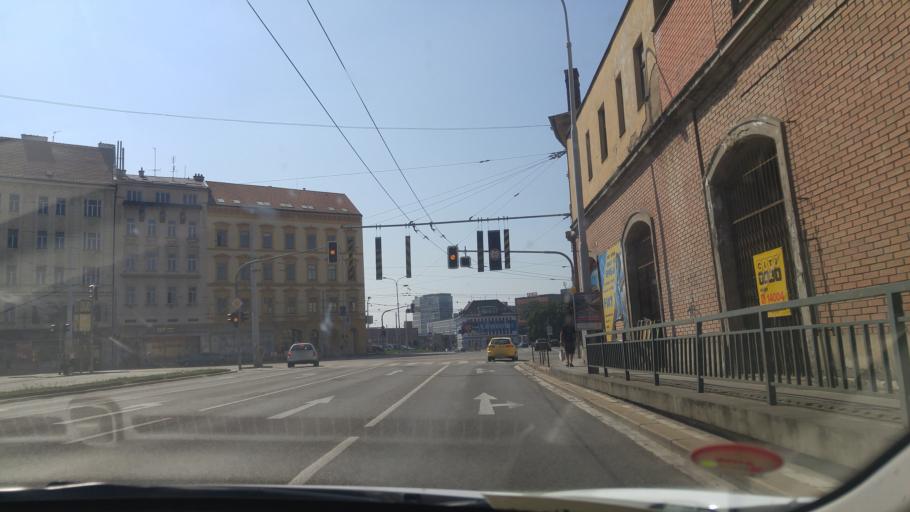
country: CZ
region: South Moravian
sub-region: Mesto Brno
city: Brno
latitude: 49.1923
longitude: 16.6152
